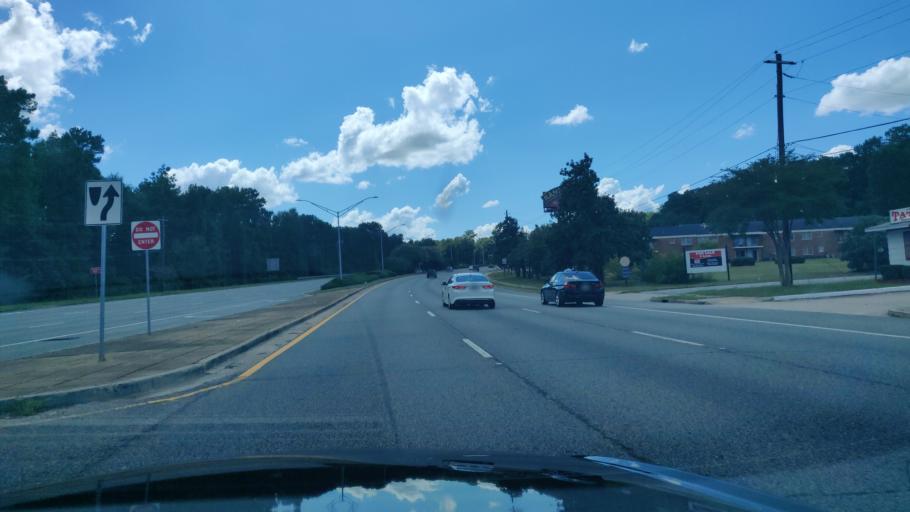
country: US
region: Georgia
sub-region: Muscogee County
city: Columbus
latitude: 32.4054
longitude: -84.9333
